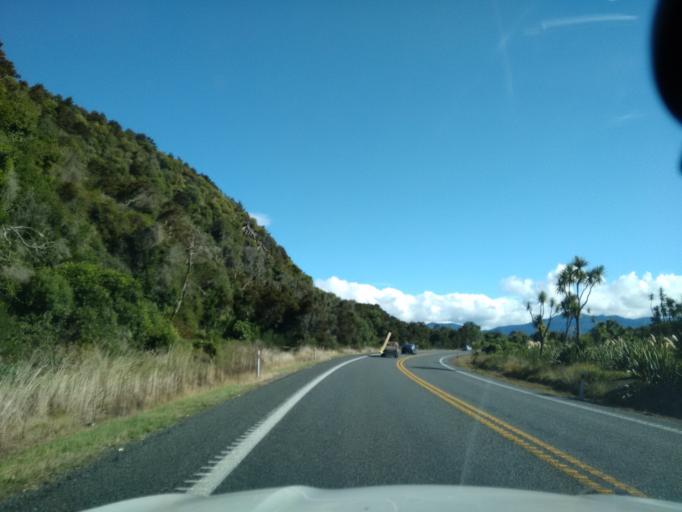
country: NZ
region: Waikato
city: Turangi
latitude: -38.9431
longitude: 175.8555
